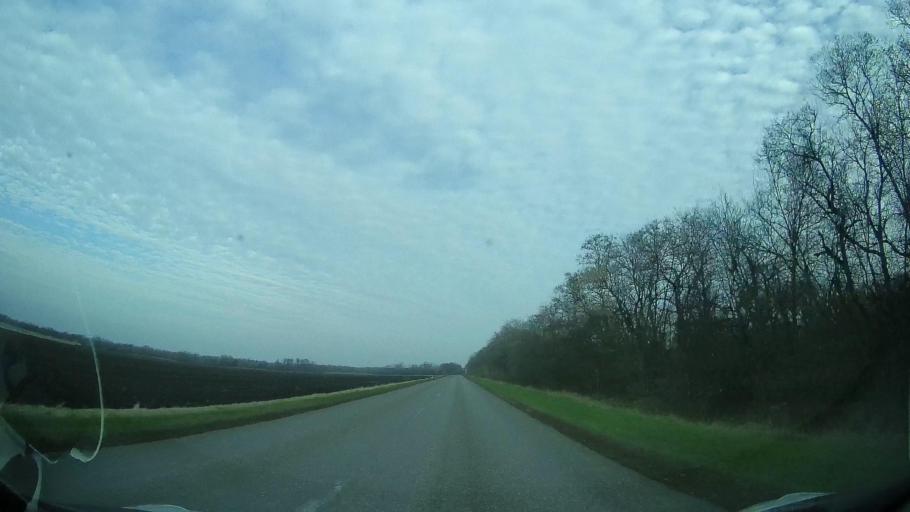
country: RU
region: Rostov
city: Zernograd
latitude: 46.9655
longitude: 40.3827
